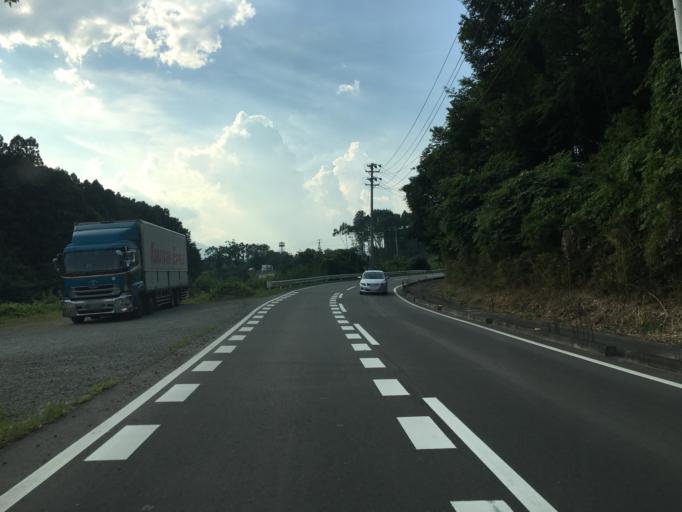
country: JP
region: Fukushima
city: Nihommatsu
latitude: 37.5733
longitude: 140.4318
